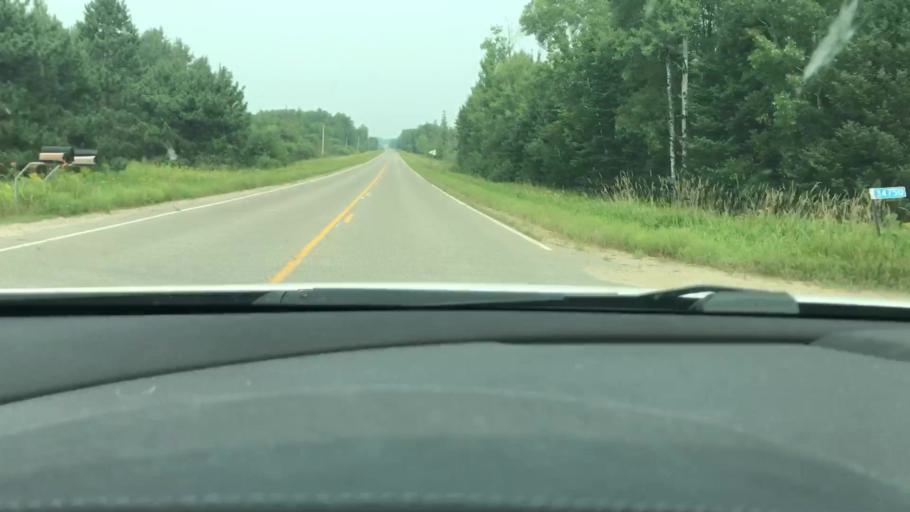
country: US
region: Minnesota
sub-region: Itasca County
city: Cohasset
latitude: 47.3791
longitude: -93.8803
